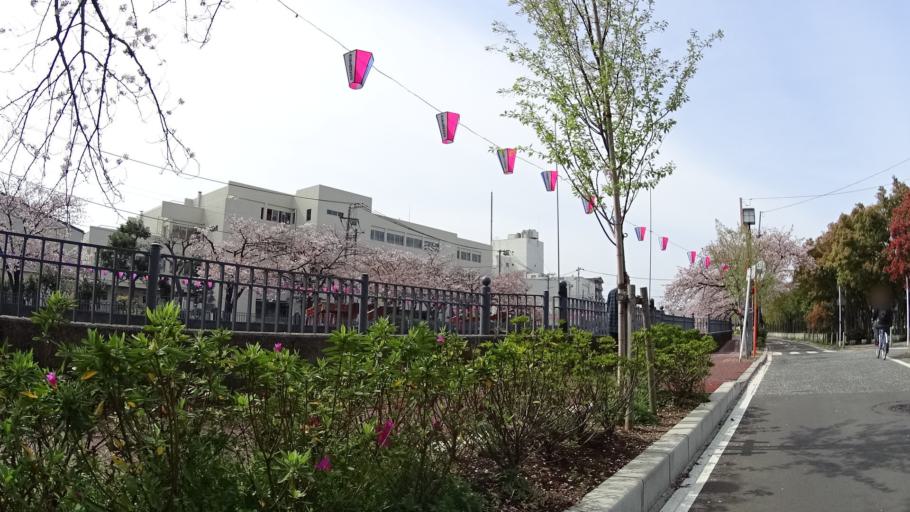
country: JP
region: Kanagawa
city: Yokohama
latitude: 35.4330
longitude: 139.6093
